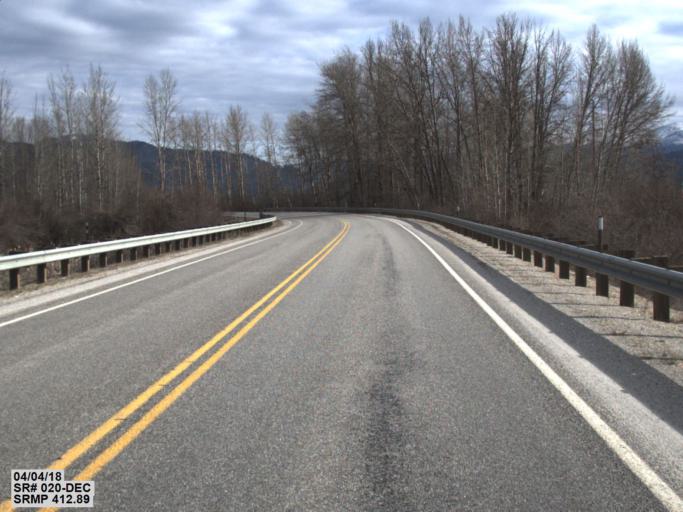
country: US
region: Washington
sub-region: Pend Oreille County
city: Newport
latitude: 48.4233
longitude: -117.3172
